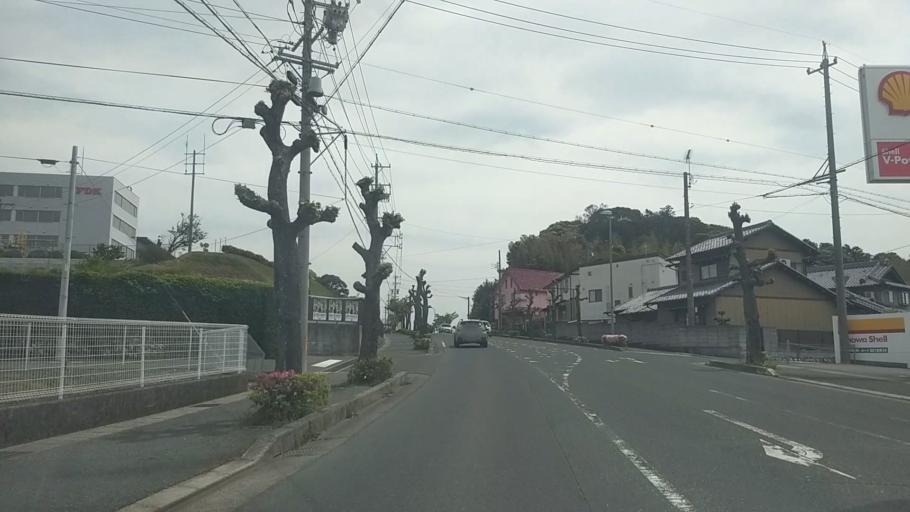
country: JP
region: Shizuoka
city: Kosai-shi
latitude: 34.7149
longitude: 137.5363
